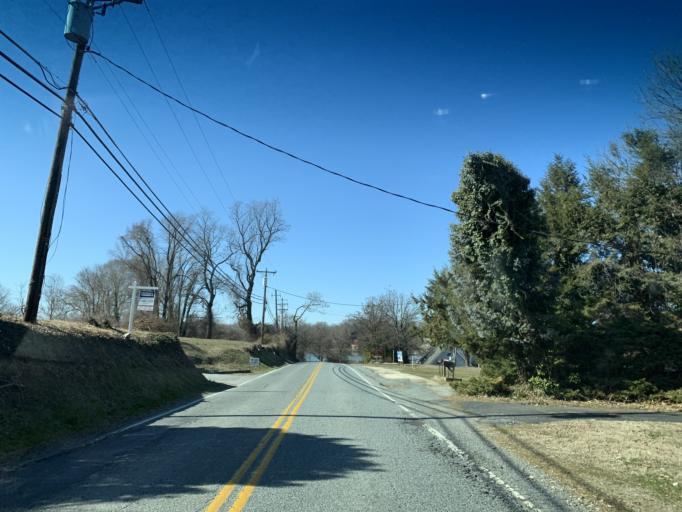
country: US
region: Maryland
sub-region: Cecil County
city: Elkton
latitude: 39.4601
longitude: -75.8735
